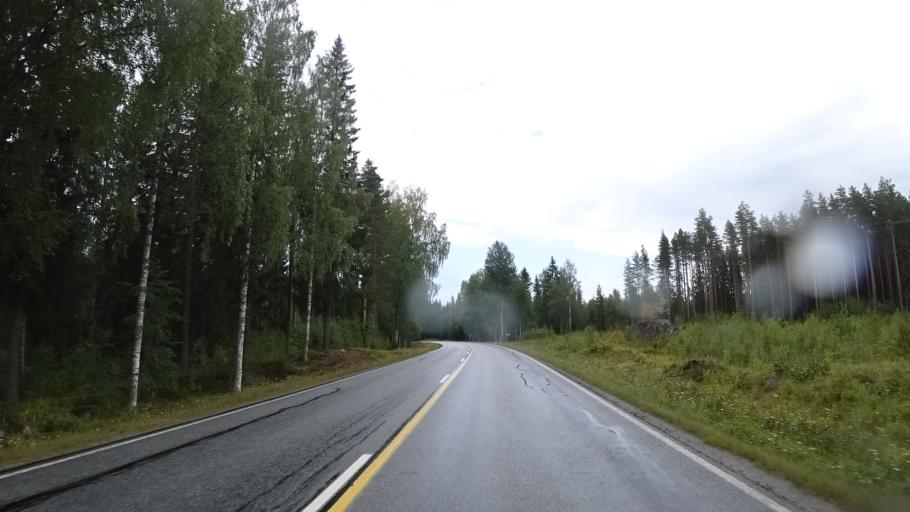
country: FI
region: North Karelia
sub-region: Keski-Karjala
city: Raeaekkylae
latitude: 62.0820
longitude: 29.6589
